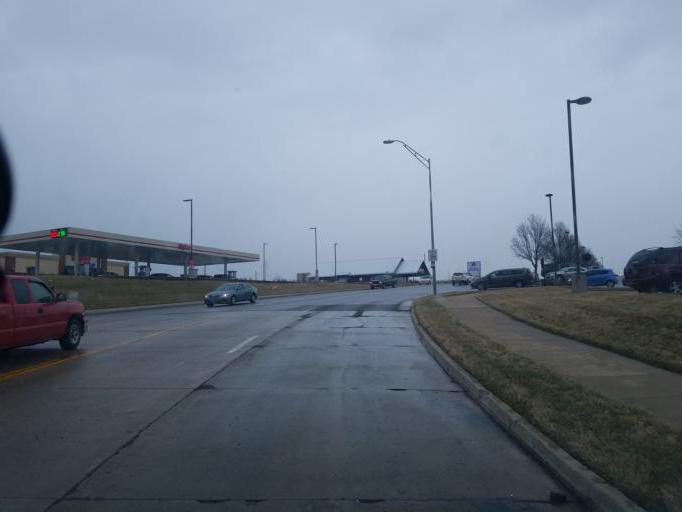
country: US
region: Missouri
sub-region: Boone County
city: Columbia
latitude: 38.9476
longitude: -92.2992
